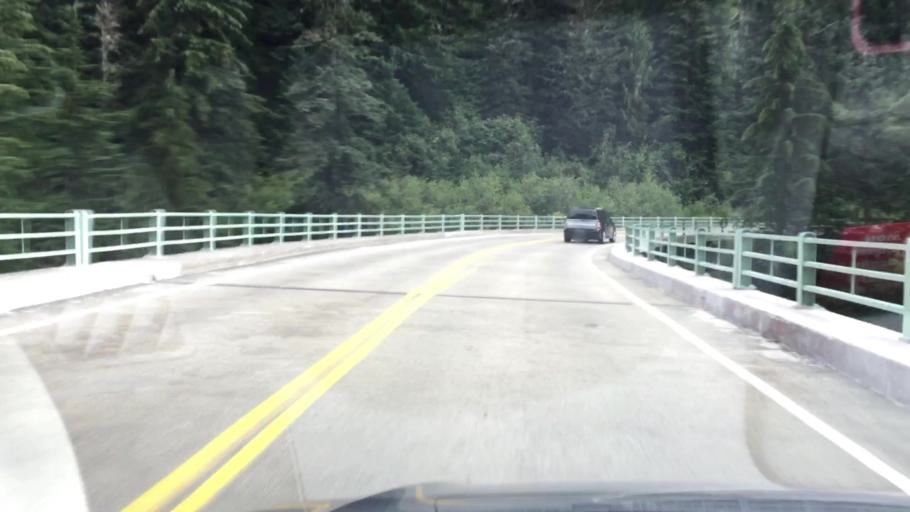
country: US
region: Washington
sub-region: Pierce County
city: Buckley
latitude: 46.7816
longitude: -121.7619
